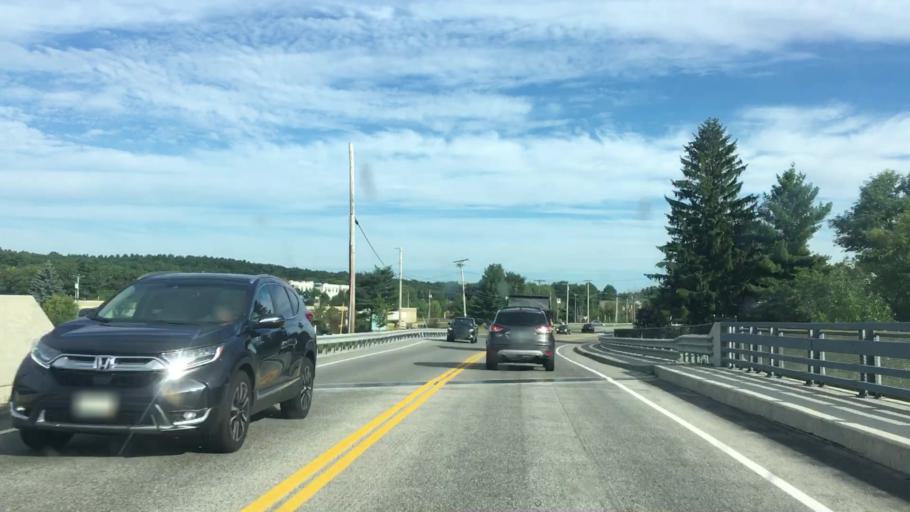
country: US
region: Maine
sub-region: Cumberland County
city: Falmouth
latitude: 43.7303
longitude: -70.2956
